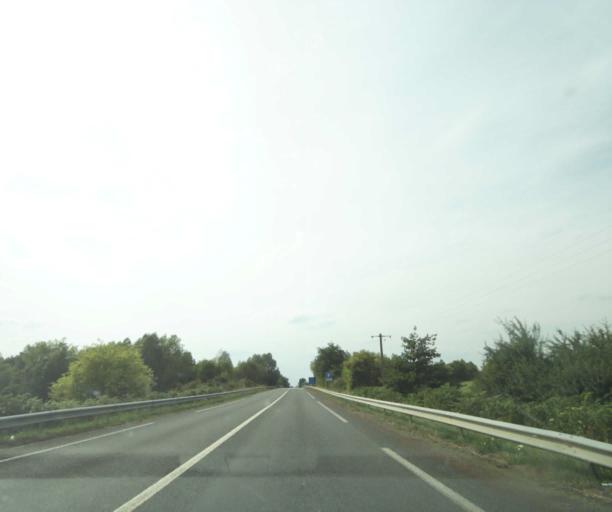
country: FR
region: Pays de la Loire
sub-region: Departement de la Sarthe
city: Marigne-Laille
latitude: 47.8129
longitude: 0.3092
